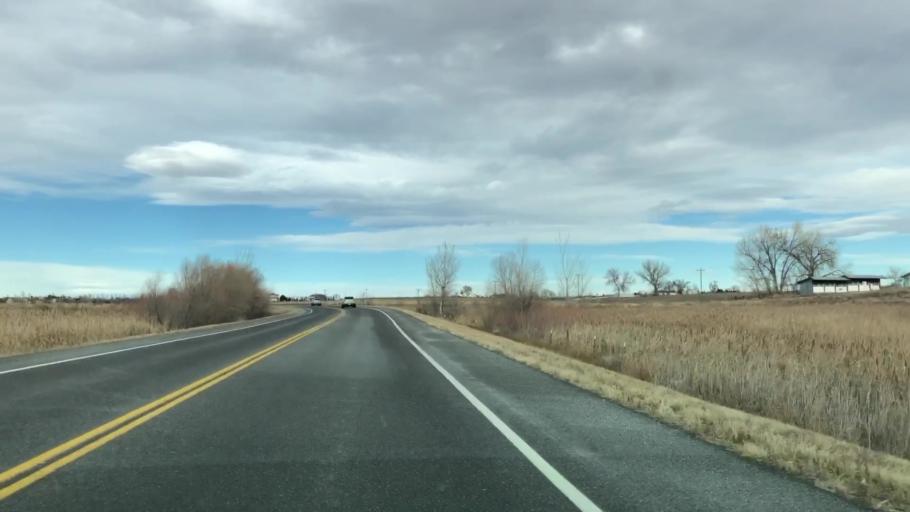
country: US
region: Colorado
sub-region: Weld County
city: Windsor
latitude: 40.5137
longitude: -104.9271
